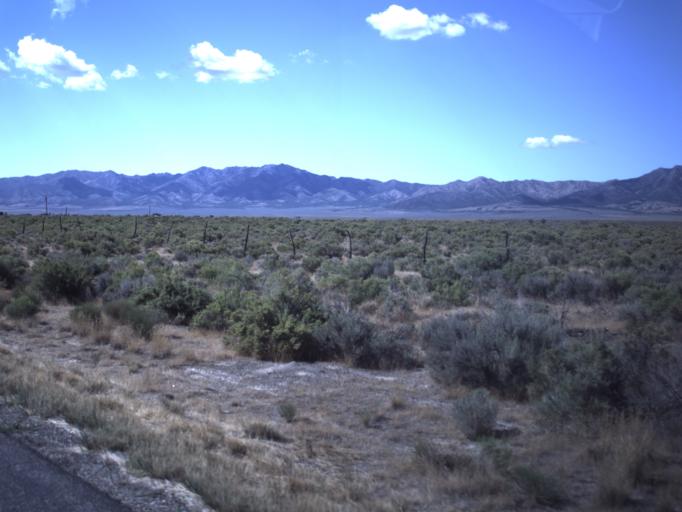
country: US
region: Utah
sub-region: Tooele County
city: Tooele
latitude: 40.1227
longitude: -112.4308
